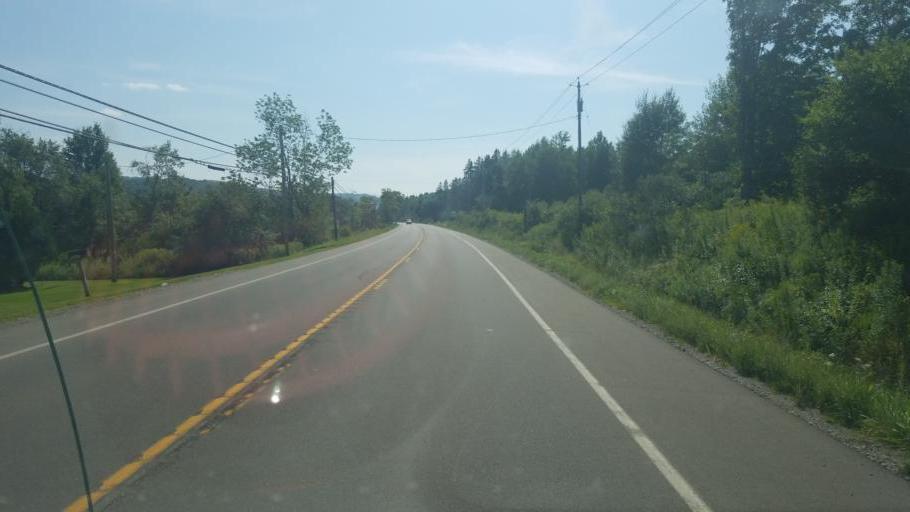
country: US
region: New York
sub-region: Allegany County
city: Wellsville
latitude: 42.0974
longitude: -78.0489
